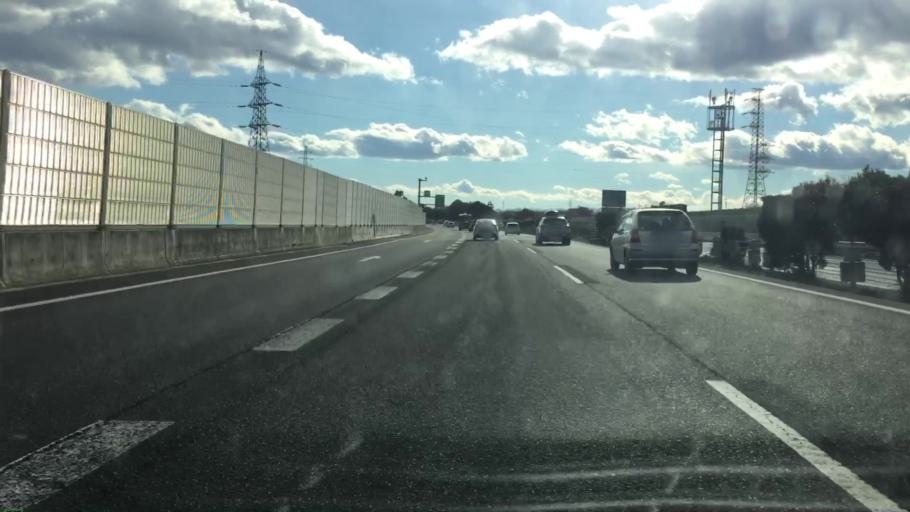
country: JP
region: Gunma
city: Shibukawa
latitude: 36.4704
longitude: 139.0126
